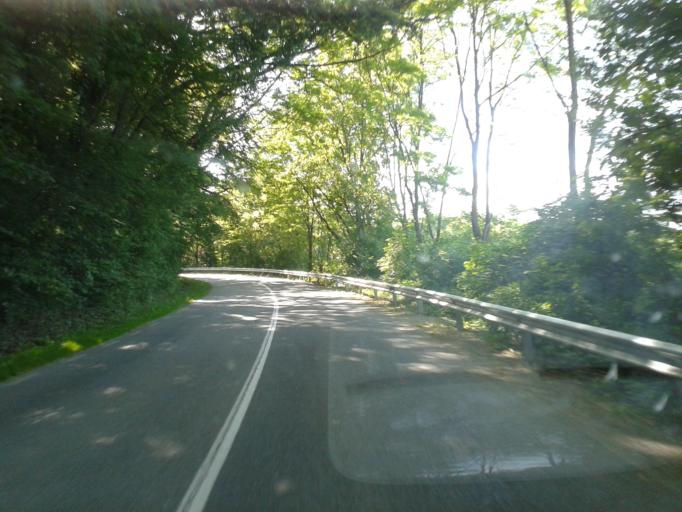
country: RO
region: Hunedoara
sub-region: Comuna Geoagiu
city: Geoagiu
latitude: 45.9415
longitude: 23.1769
